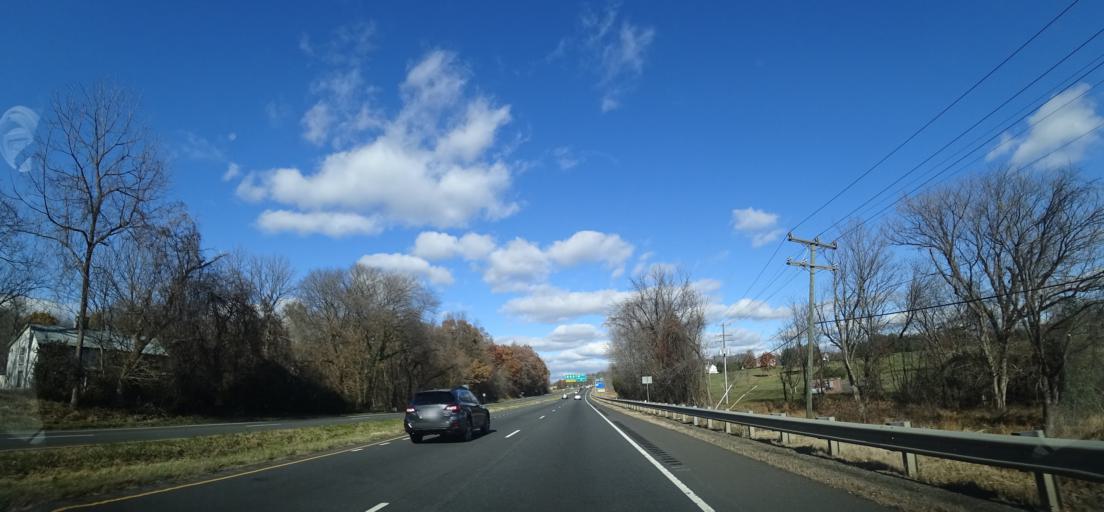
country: US
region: Virginia
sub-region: Fauquier County
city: Warrenton
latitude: 38.6798
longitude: -77.7871
